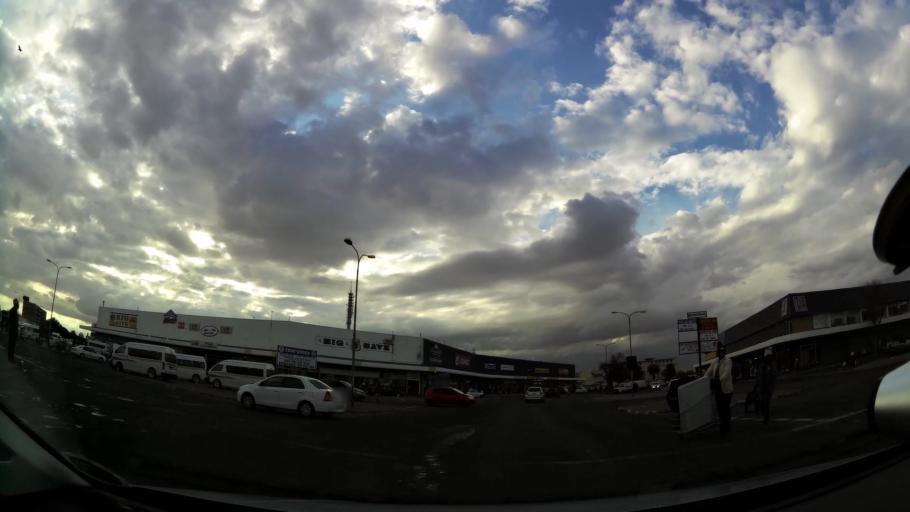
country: ZA
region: Orange Free State
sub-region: Lejweleputswa District Municipality
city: Welkom
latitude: -27.9830
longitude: 26.7346
